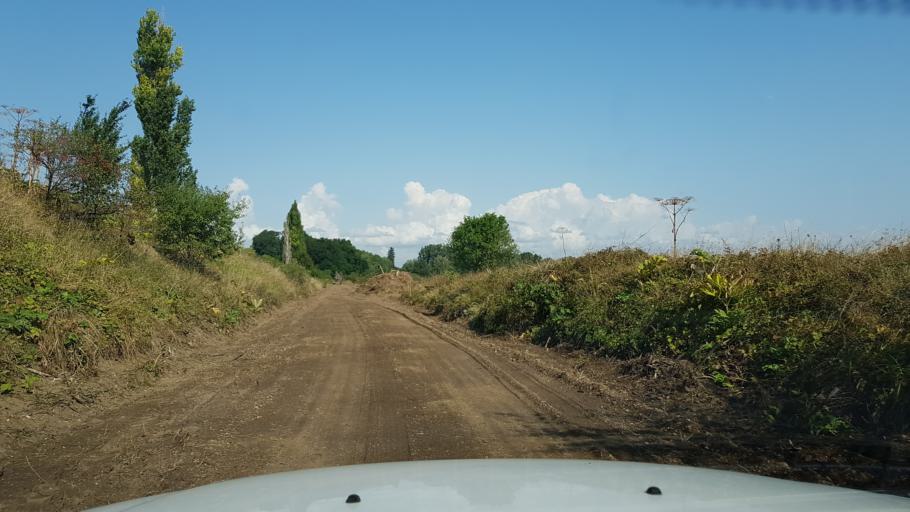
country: PL
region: West Pomeranian Voivodeship
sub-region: Powiat choszczenski
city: Pelczyce
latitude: 53.0808
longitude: 15.3031
